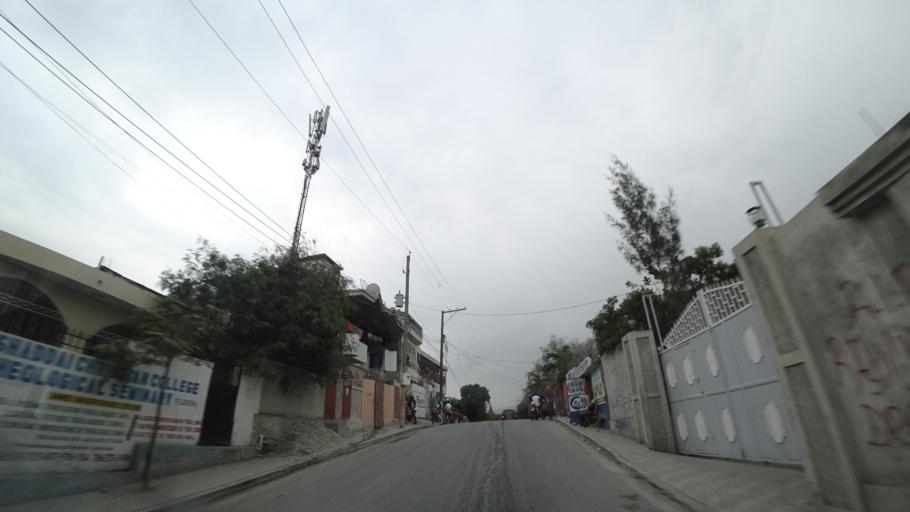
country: HT
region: Ouest
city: Delmas 73
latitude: 18.5635
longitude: -72.2960
